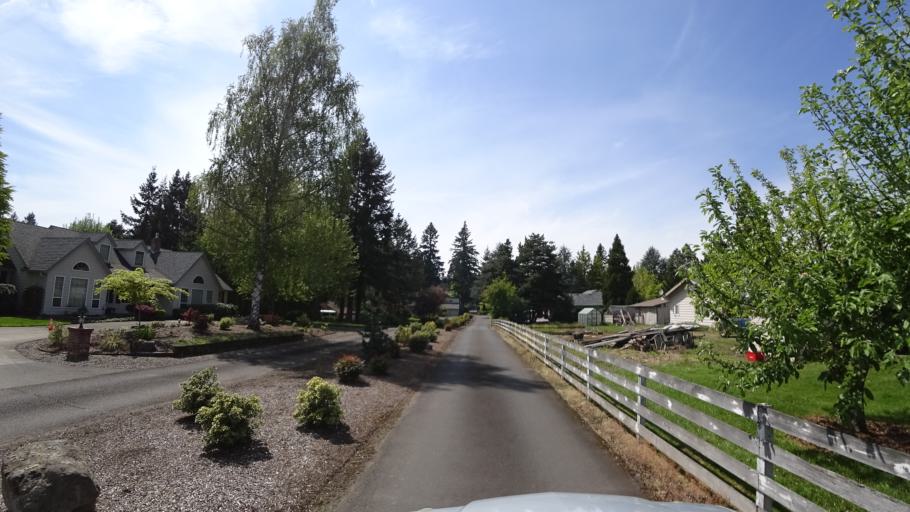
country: US
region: Oregon
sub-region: Washington County
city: Hillsboro
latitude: 45.5103
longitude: -122.9374
